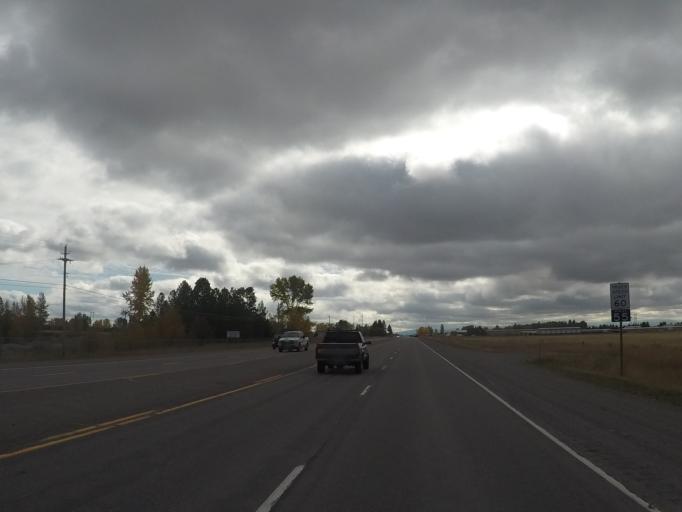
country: US
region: Montana
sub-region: Flathead County
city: Columbia Falls
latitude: 48.3676
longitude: -114.2410
